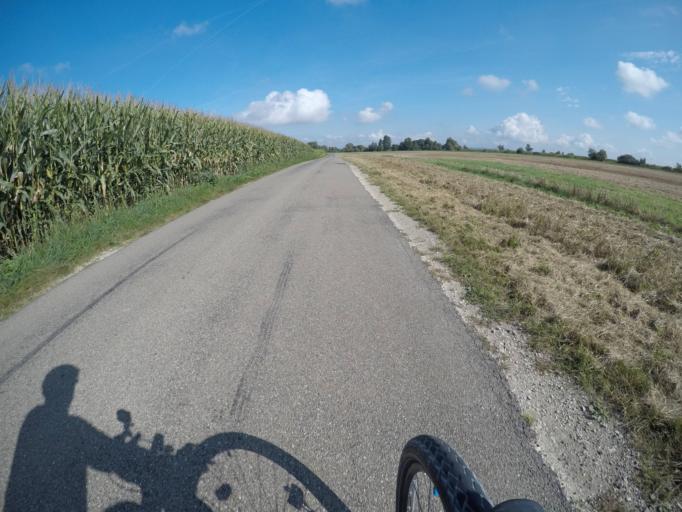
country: DE
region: Bavaria
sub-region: Swabia
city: Buttenwiesen
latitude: 48.6515
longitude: 10.7341
